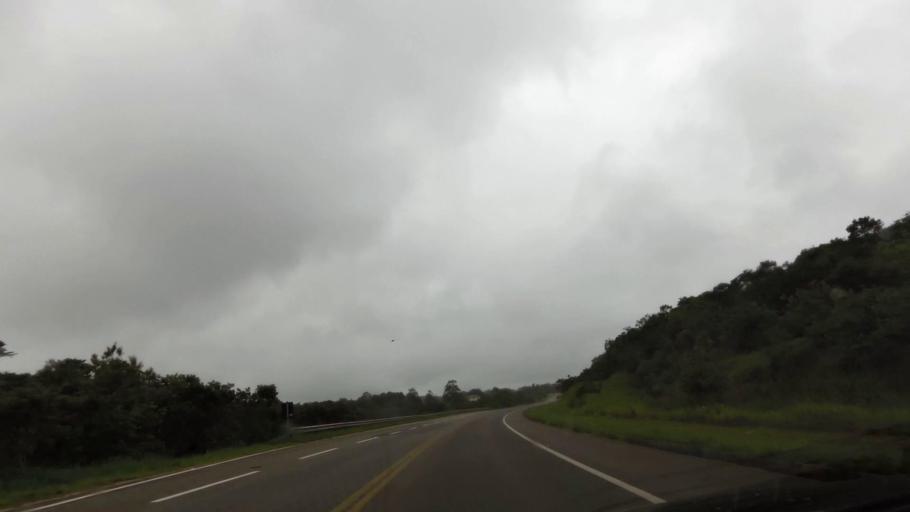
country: BR
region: Espirito Santo
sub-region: Guarapari
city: Guarapari
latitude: -20.7092
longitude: -40.5760
